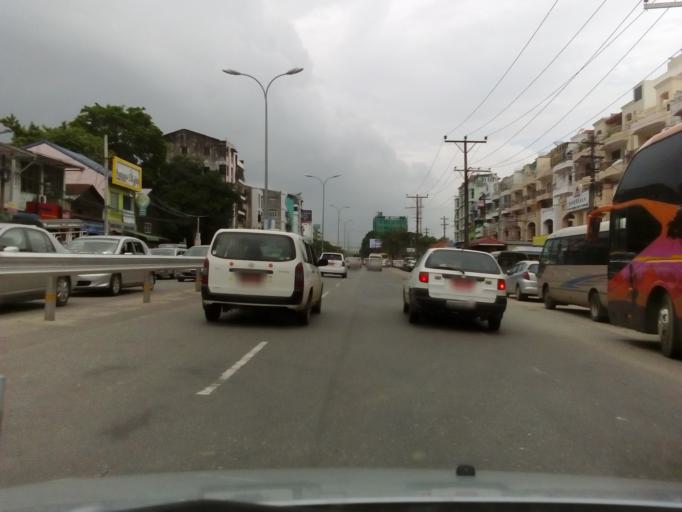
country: MM
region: Yangon
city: Yangon
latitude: 16.8152
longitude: 96.1686
